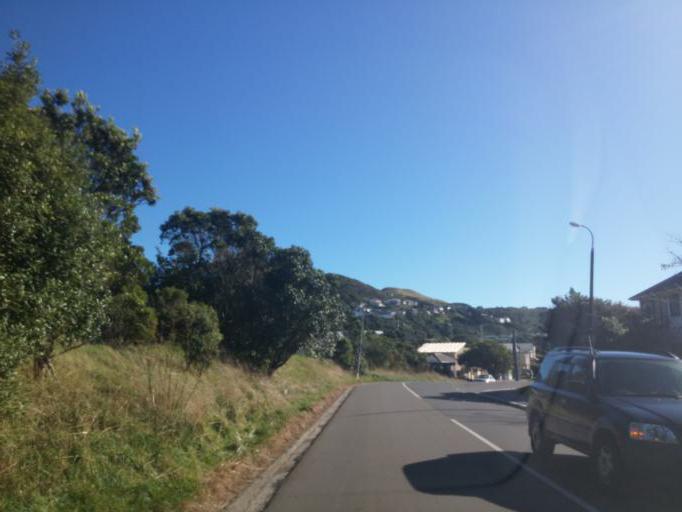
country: NZ
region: Wellington
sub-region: Wellington City
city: Wellington
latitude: -41.2293
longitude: 174.8000
